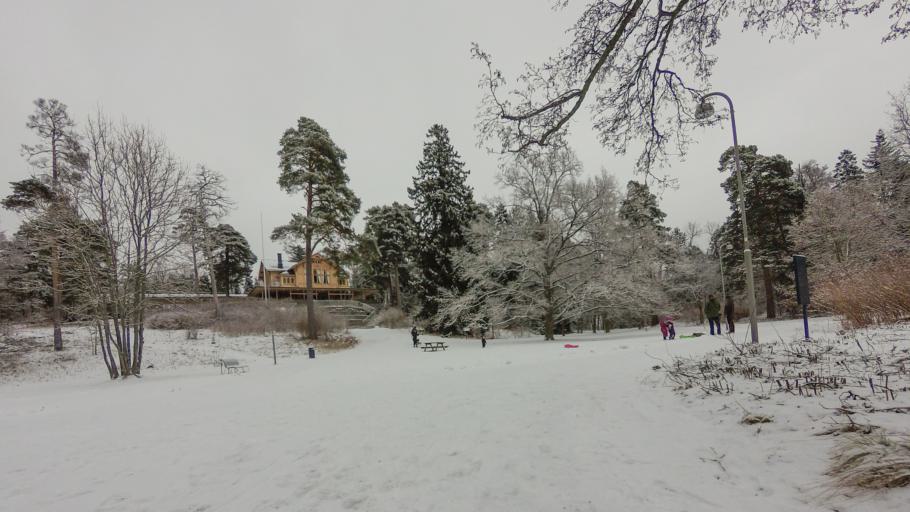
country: FI
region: Uusimaa
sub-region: Helsinki
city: Teekkarikylae
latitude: 60.1807
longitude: 24.8820
